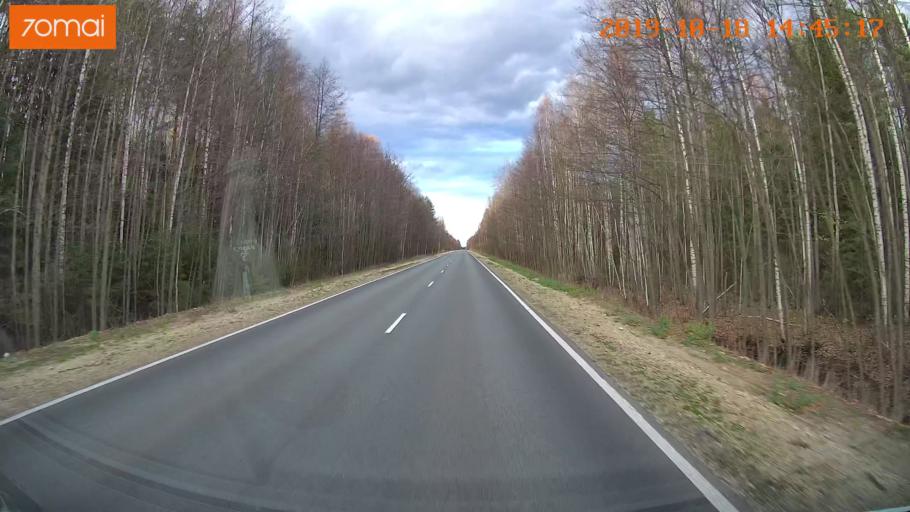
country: RU
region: Vladimir
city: Velikodvorskiy
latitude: 55.3525
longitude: 40.6786
